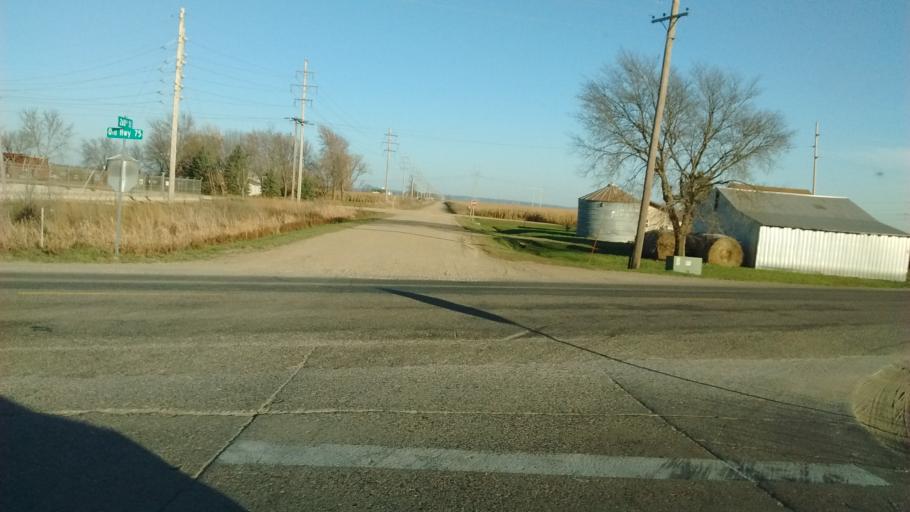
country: US
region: Iowa
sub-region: Woodbury County
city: Sergeant Bluff
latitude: 42.3302
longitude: -96.3020
